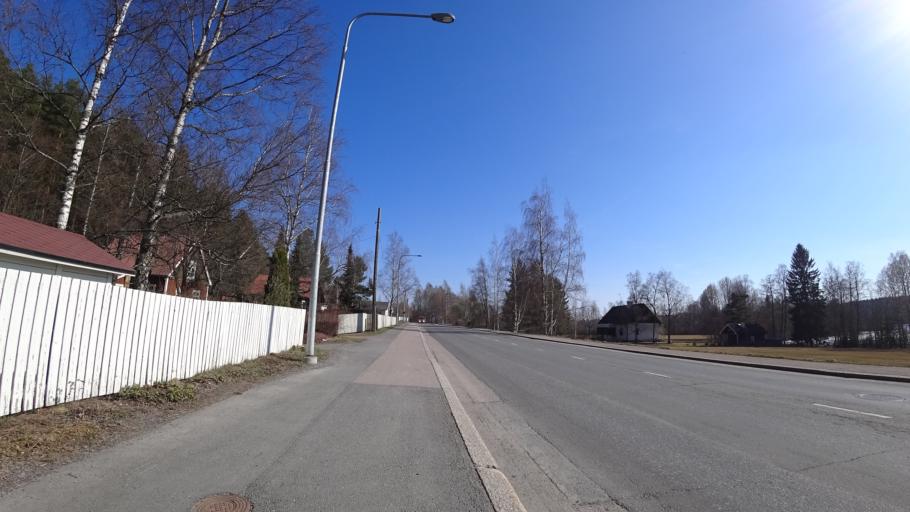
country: FI
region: Pirkanmaa
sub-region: Tampere
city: Pirkkala
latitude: 61.5149
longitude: 23.6520
